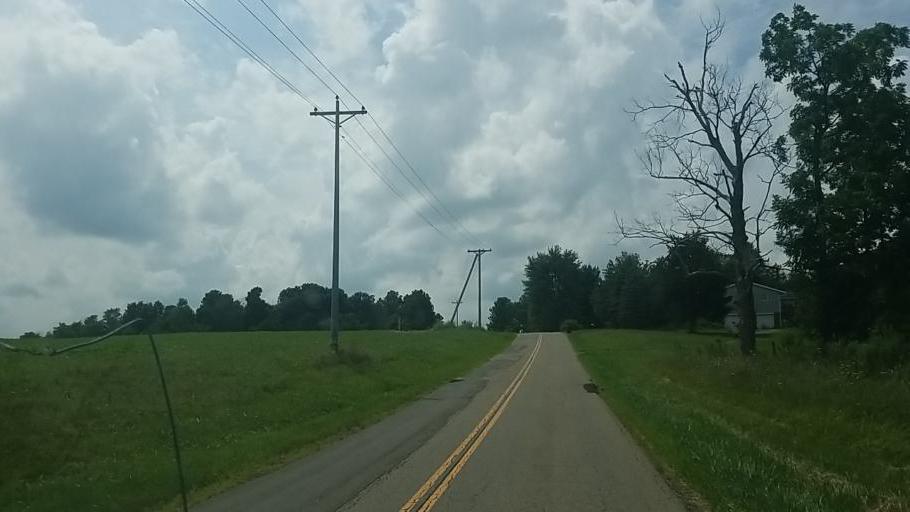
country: US
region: Ohio
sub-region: Knox County
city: Gambier
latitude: 40.3212
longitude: -82.4467
